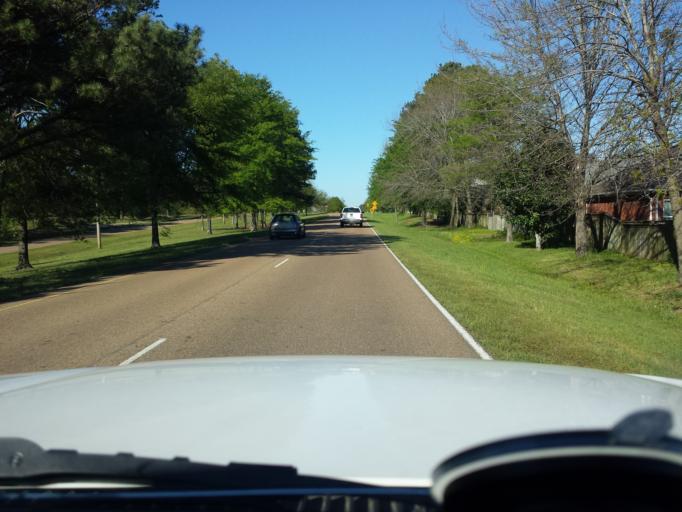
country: US
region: Mississippi
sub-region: Madison County
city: Ridgeland
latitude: 32.3866
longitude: -90.0375
